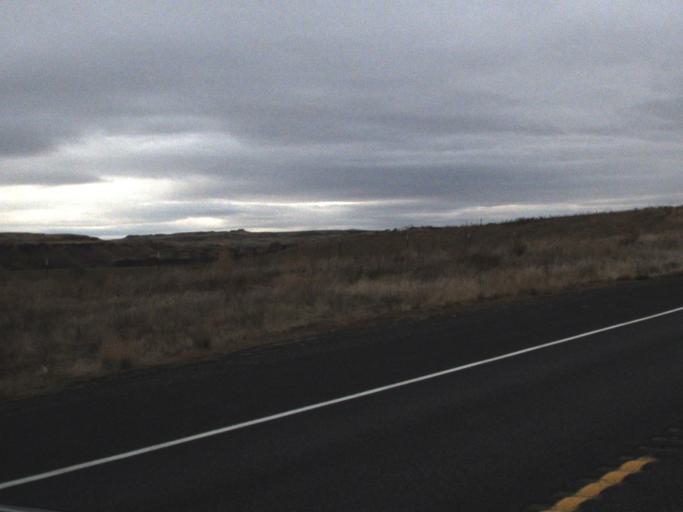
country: US
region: Washington
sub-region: Columbia County
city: Dayton
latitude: 46.7748
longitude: -118.0461
